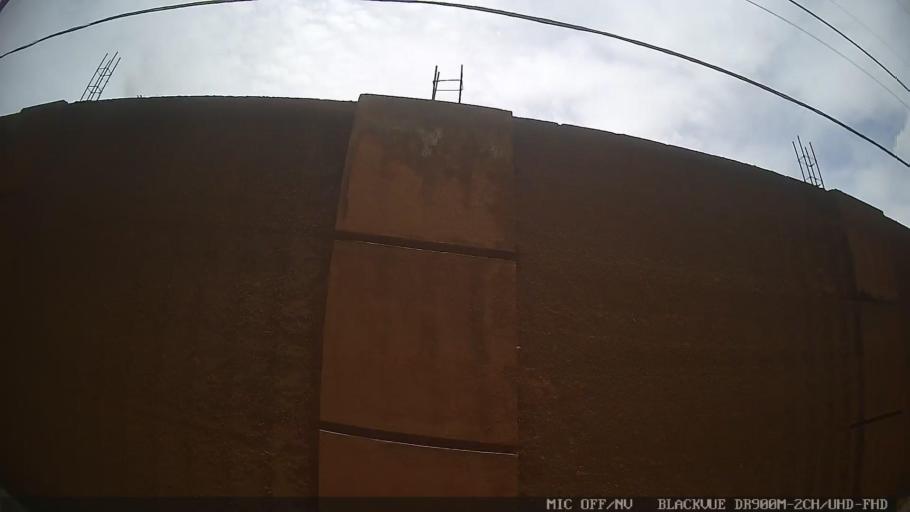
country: BR
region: Sao Paulo
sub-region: Santa Isabel
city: Santa Isabel
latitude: -23.3566
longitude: -46.2278
